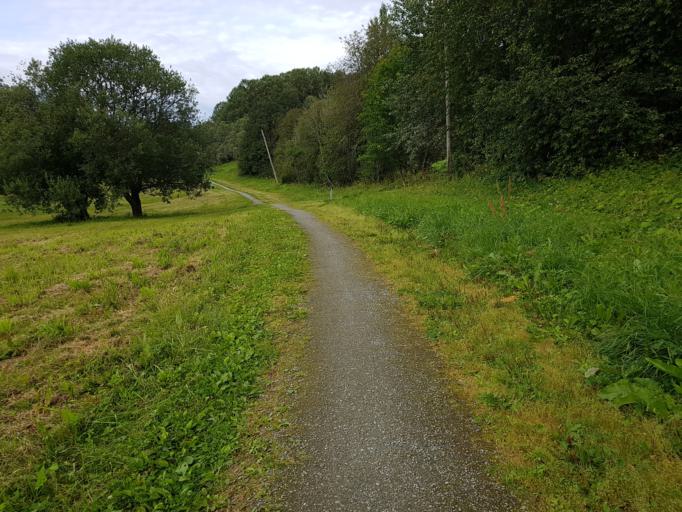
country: NO
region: Sor-Trondelag
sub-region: Trondheim
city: Trondheim
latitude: 63.4024
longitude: 10.4433
